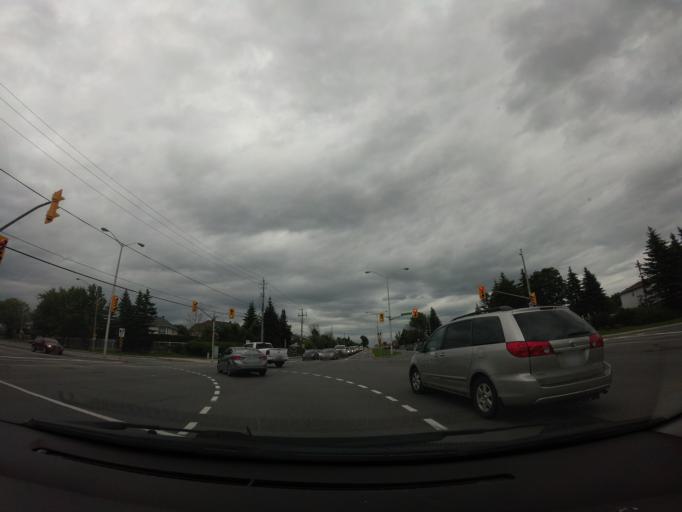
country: CA
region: Ontario
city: Ottawa
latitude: 45.4443
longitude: -75.5330
